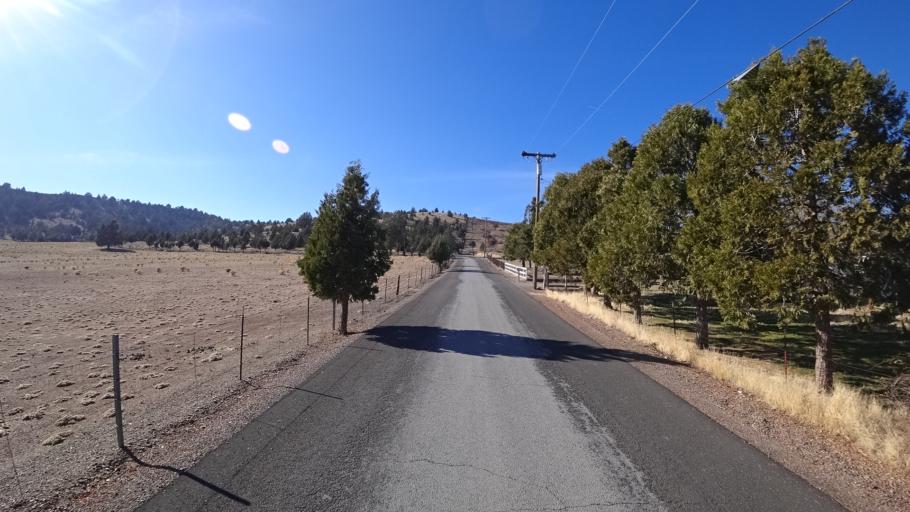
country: US
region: California
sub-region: Siskiyou County
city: Montague
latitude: 41.6327
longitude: -122.5382
